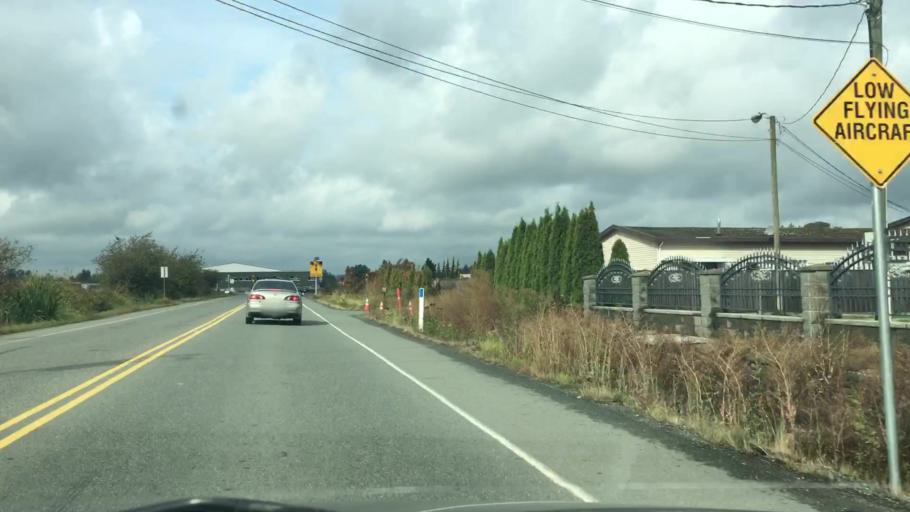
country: CA
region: British Columbia
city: Langley
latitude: 49.1040
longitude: -122.6218
